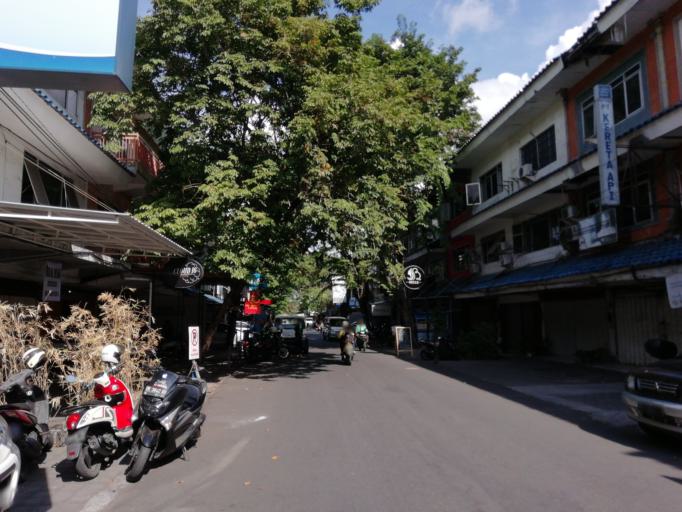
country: ID
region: Bali
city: Denpasar
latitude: -8.6702
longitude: 115.2152
